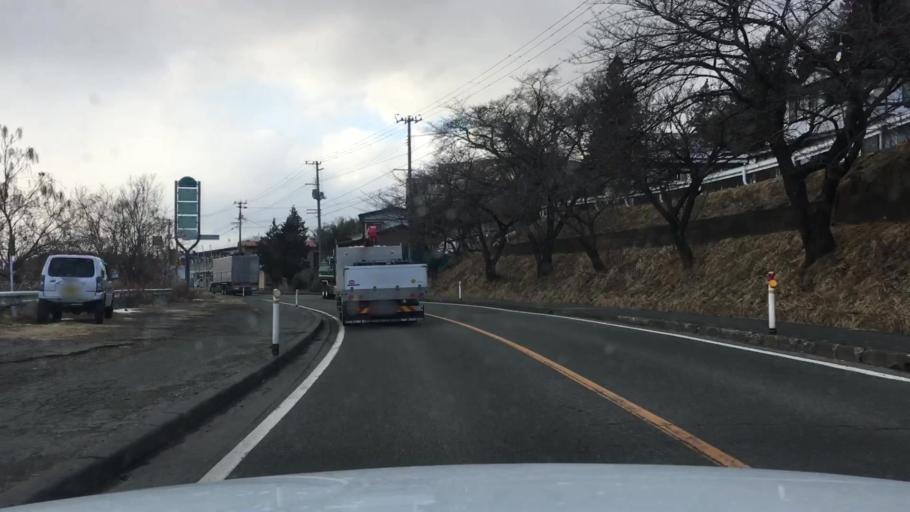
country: JP
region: Iwate
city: Morioka-shi
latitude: 39.6869
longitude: 141.1813
